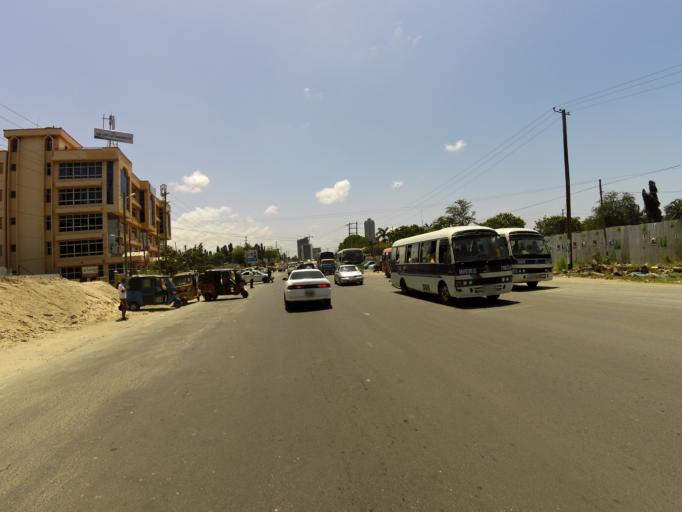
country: TZ
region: Dar es Salaam
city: Magomeni
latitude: -6.7785
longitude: 39.2526
